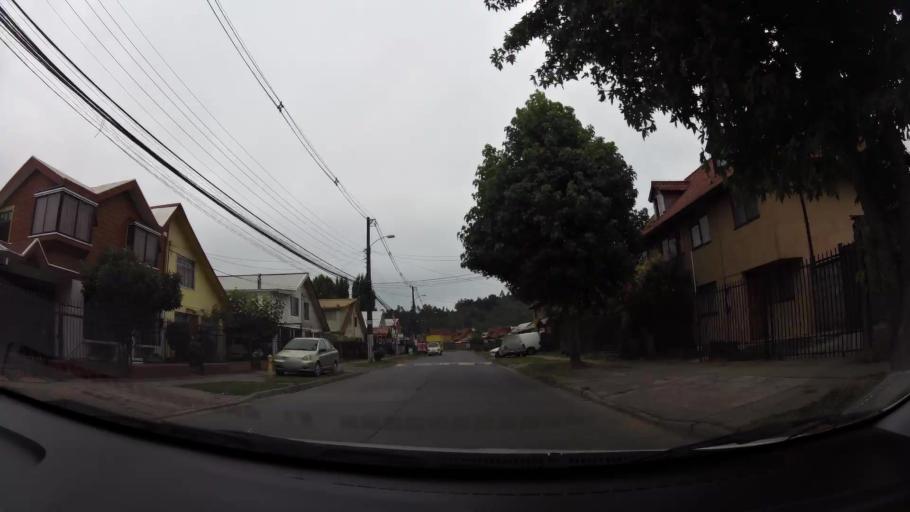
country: CL
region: Biobio
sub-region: Provincia de Concepcion
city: Concepcion
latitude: -36.8300
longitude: -73.0114
